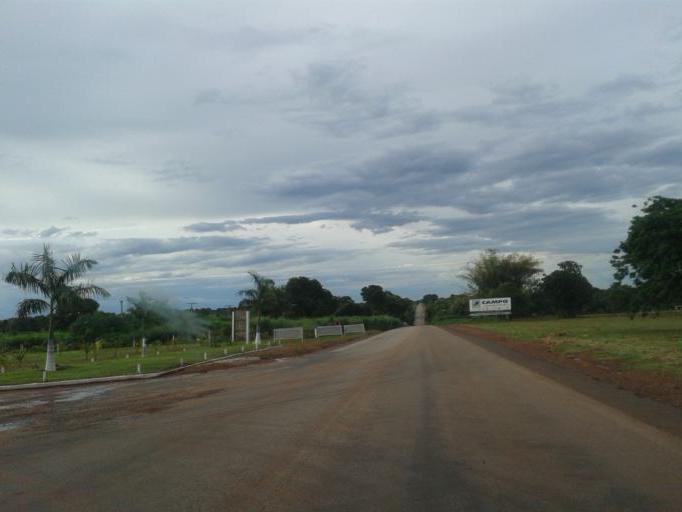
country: BR
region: Goias
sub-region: Mozarlandia
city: Mozarlandia
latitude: -14.7545
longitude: -50.5404
